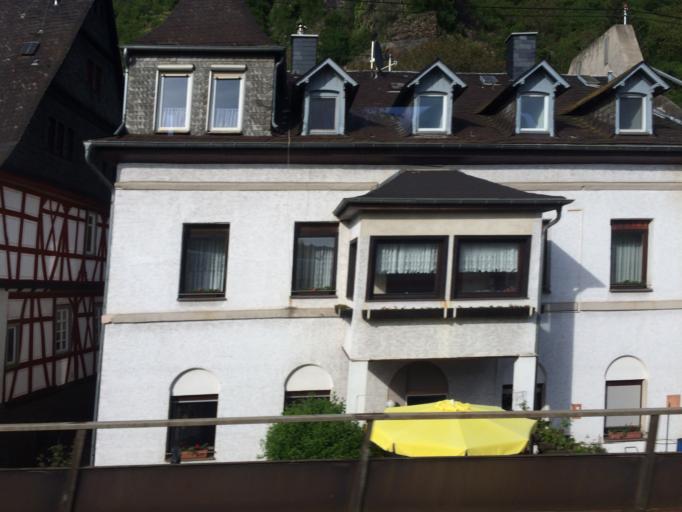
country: DE
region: Rheinland-Pfalz
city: Braubach
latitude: 50.2711
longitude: 7.6463
